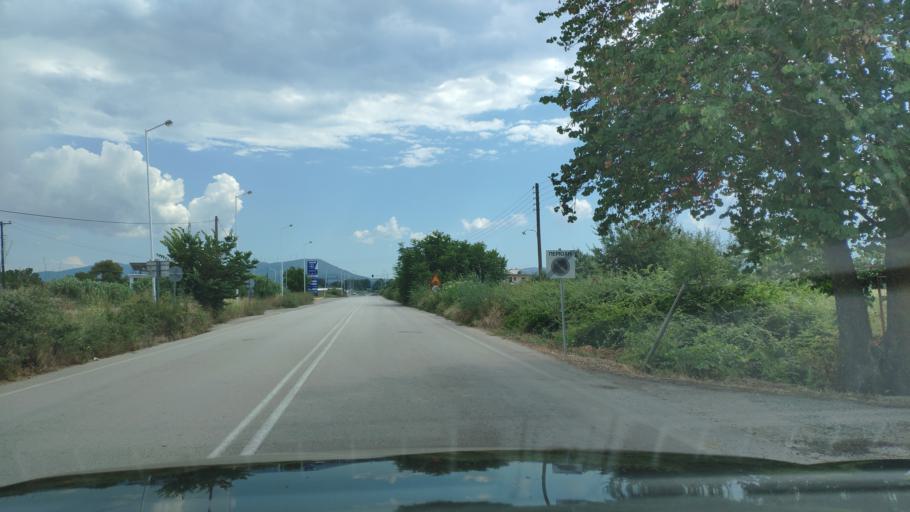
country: GR
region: West Greece
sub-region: Nomos Aitolias kai Akarnanias
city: Krikellos
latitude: 38.9344
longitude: 21.1771
